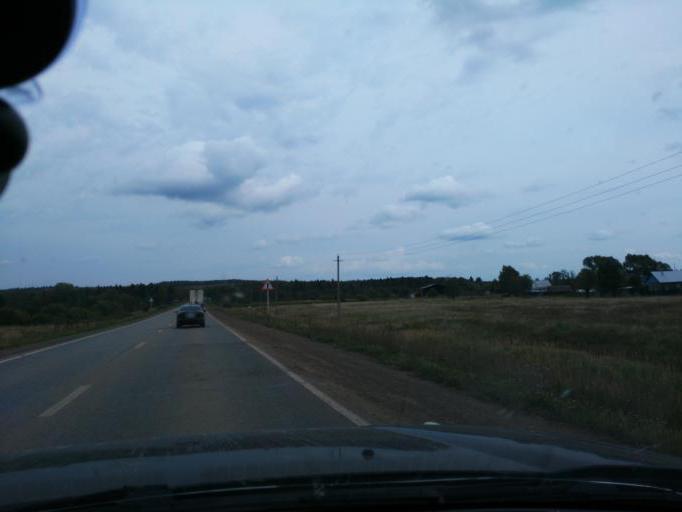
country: RU
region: Perm
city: Kuyeda
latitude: 56.4535
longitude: 55.6145
